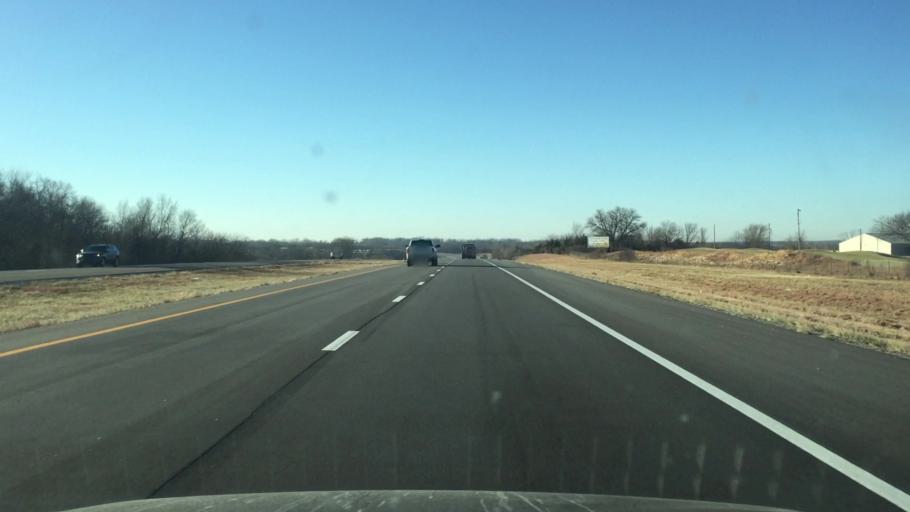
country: US
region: Kansas
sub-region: Johnson County
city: Spring Hill
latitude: 38.7622
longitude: -94.8322
